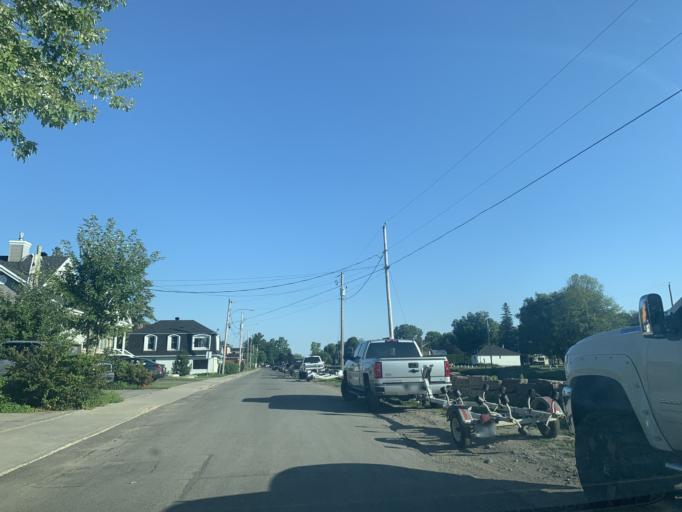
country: CA
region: Ontario
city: Hawkesbury
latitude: 45.6294
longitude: -74.6079
